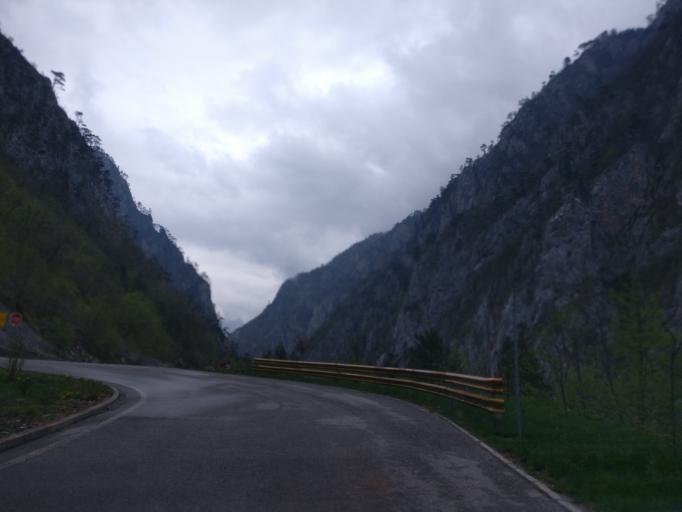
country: ME
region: Opstina Pluzine
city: Pluzine
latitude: 43.2835
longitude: 18.8496
